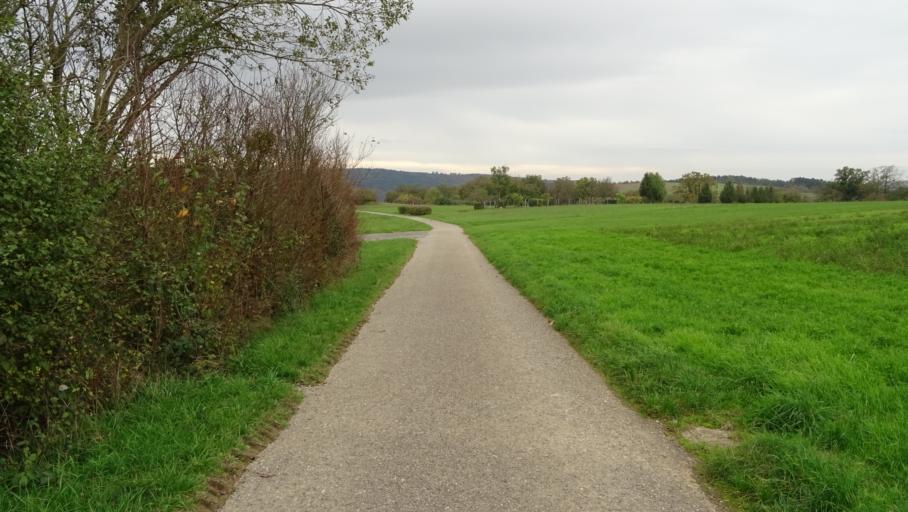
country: DE
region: Baden-Wuerttemberg
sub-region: Karlsruhe Region
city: Mosbach
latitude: 49.3633
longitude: 9.1216
